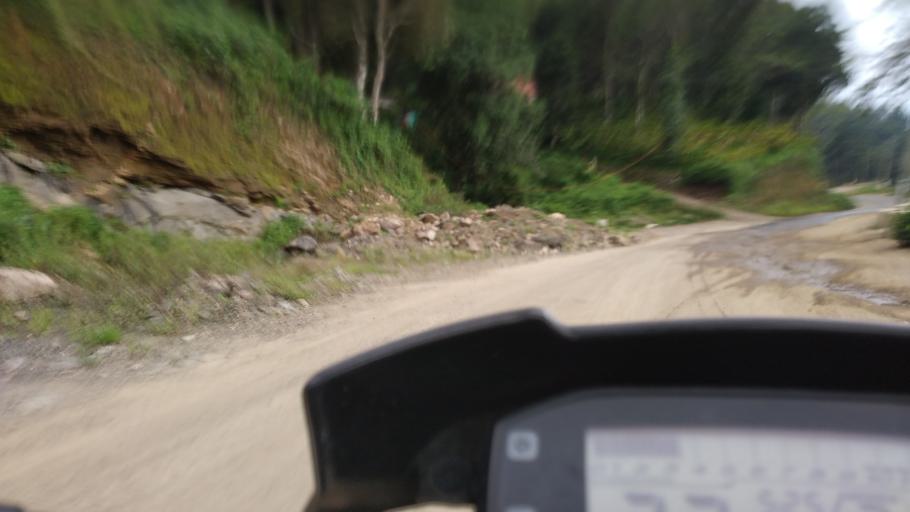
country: IN
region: Tamil Nadu
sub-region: Theni
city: Bodinayakkanur
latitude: 10.0056
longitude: 77.2276
